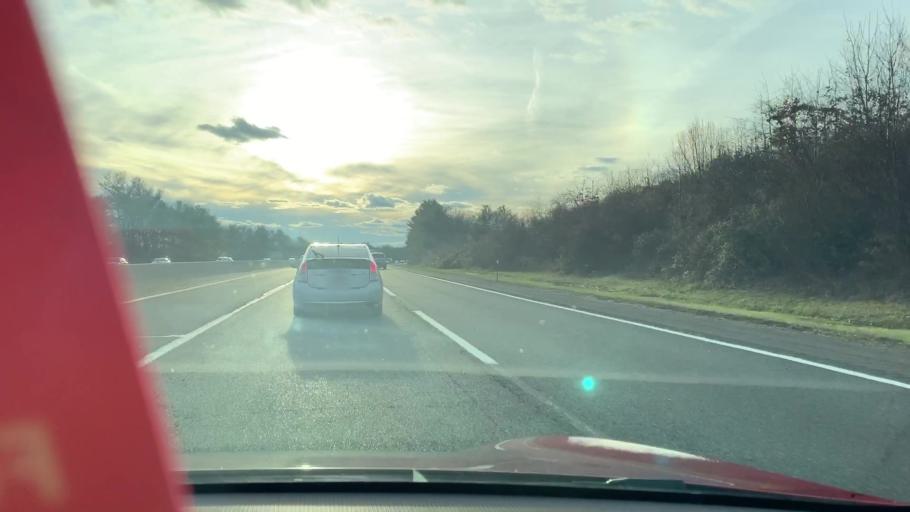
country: US
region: New Jersey
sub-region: Burlington County
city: Willingboro
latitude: 40.0083
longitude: -74.8416
